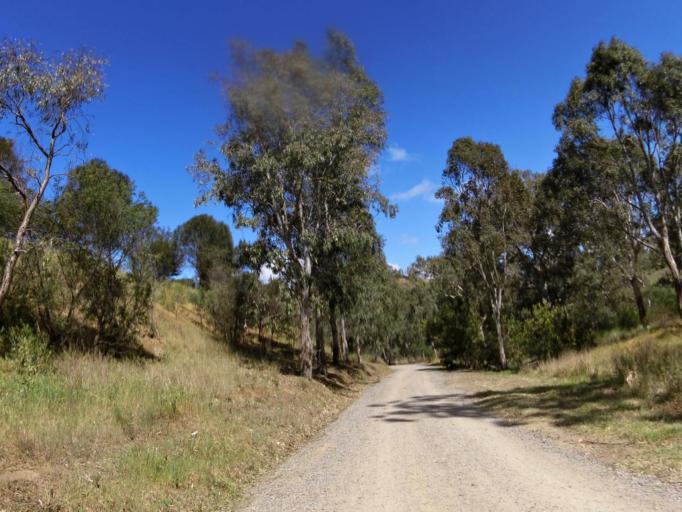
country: AU
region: Victoria
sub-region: Brimbank
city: Kealba
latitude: -37.7393
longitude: 144.8343
